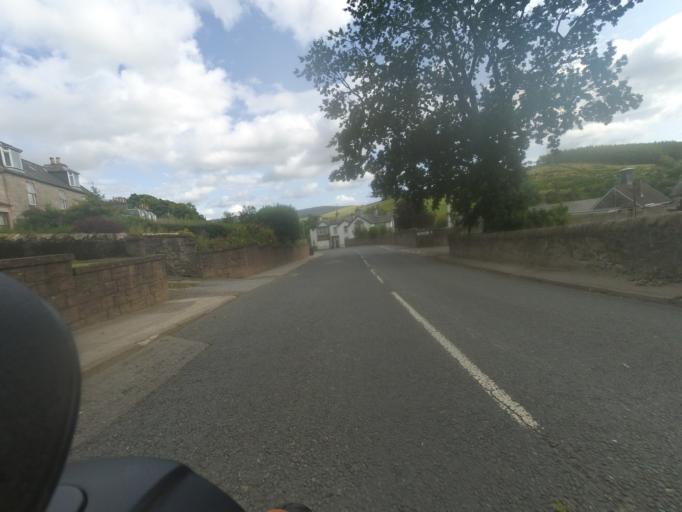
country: GB
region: Scotland
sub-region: Moray
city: Dufftown
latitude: 57.4444
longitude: -3.1236
